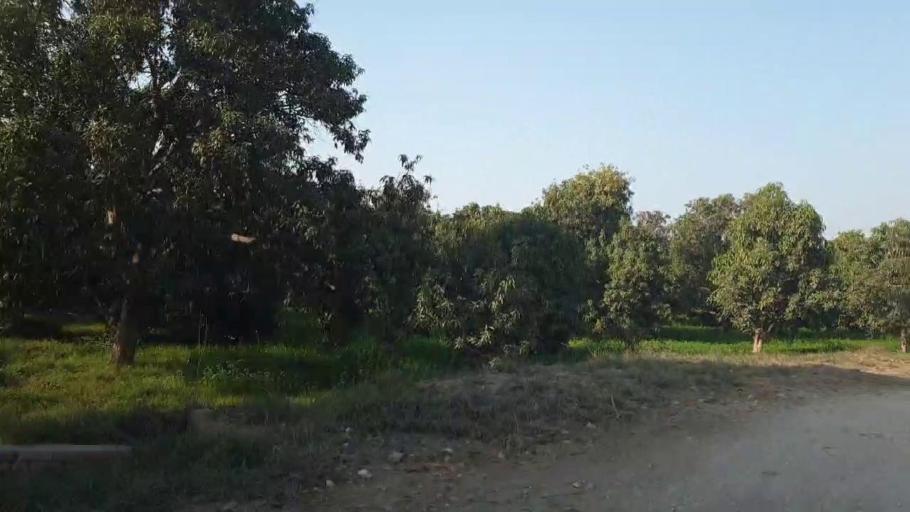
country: PK
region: Sindh
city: Mirpur Khas
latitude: 25.4381
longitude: 68.9094
